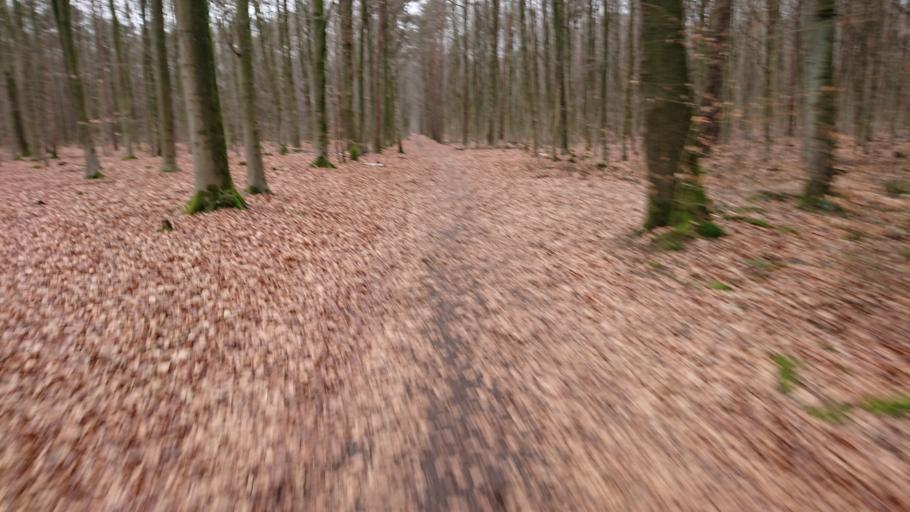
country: DE
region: North Rhine-Westphalia
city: Opladen
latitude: 51.0128
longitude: 7.0530
